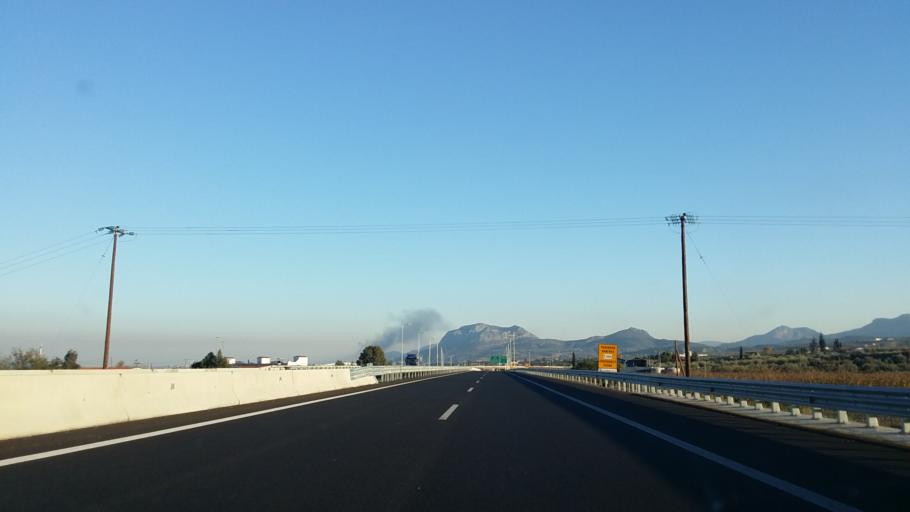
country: GR
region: Peloponnese
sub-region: Nomos Korinthias
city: Zevgolateio
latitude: 37.9328
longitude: 22.7809
